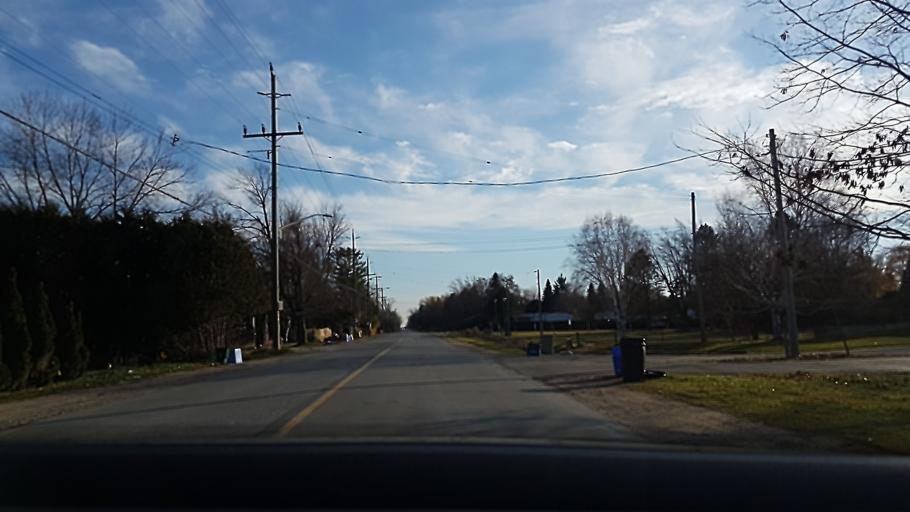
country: CA
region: Ontario
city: Innisfil
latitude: 44.3588
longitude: -79.5505
